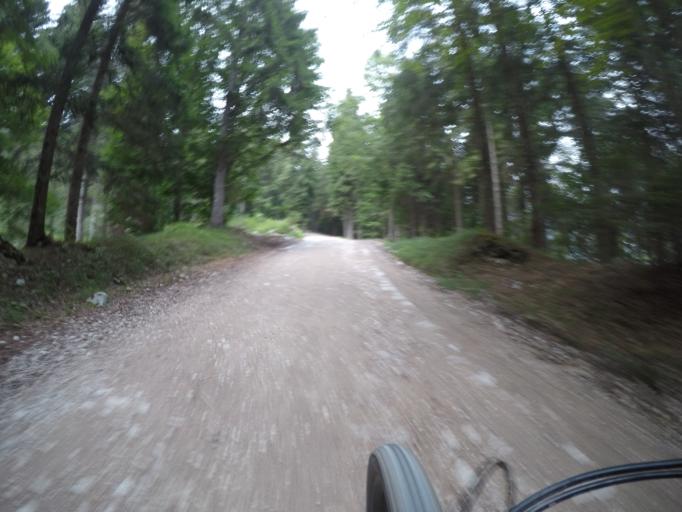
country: IT
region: Veneto
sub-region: Provincia di Vicenza
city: Gallio
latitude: 45.9107
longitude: 11.5242
